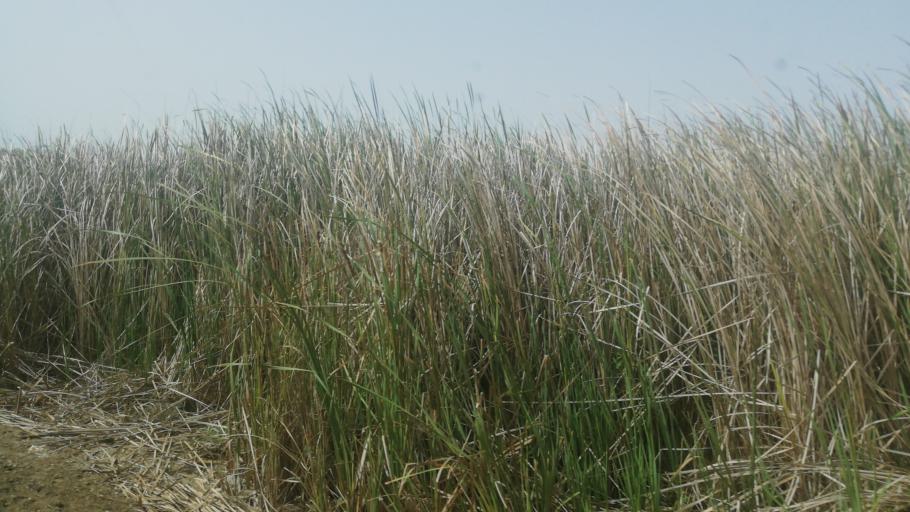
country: SN
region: Saint-Louis
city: Saint-Louis
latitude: 16.0647
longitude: -16.3177
